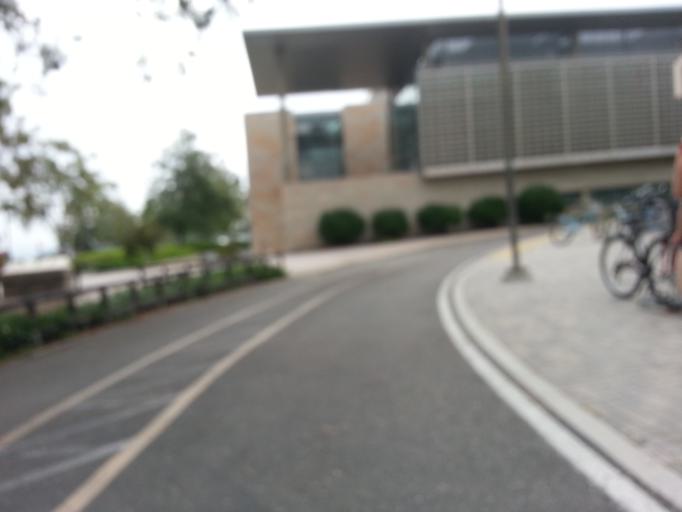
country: US
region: California
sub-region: Santa Barbara County
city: Isla Vista
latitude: 34.4158
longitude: -119.8423
